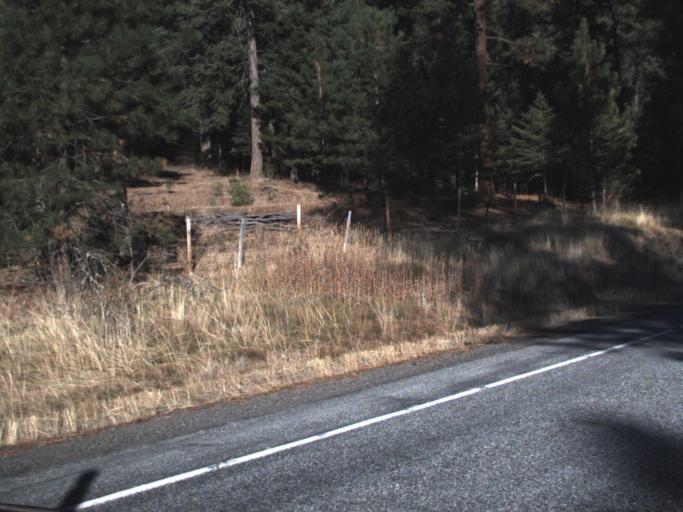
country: US
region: Washington
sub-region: Ferry County
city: Republic
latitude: 48.6009
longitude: -118.7394
